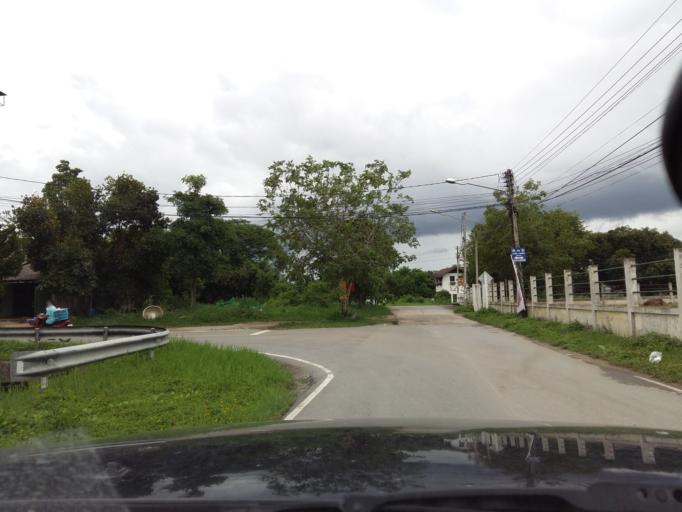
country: TH
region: Chiang Mai
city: Chiang Mai
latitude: 18.7506
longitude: 98.9808
